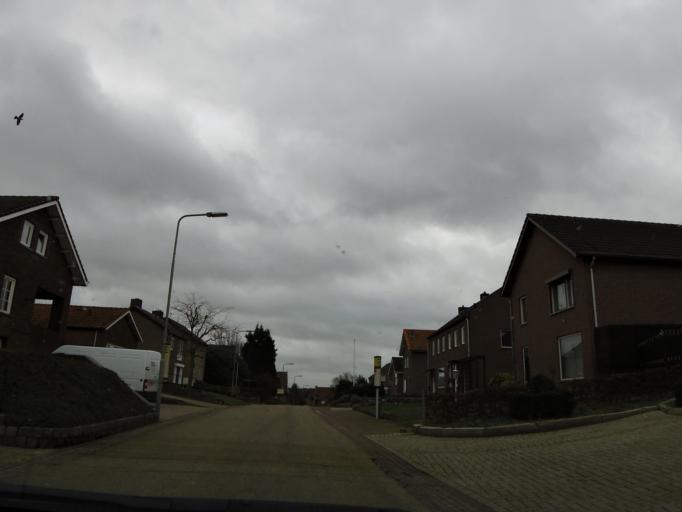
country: NL
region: Limburg
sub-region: Eijsden-Margraten
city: Margraten
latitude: 50.7949
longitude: 5.8058
